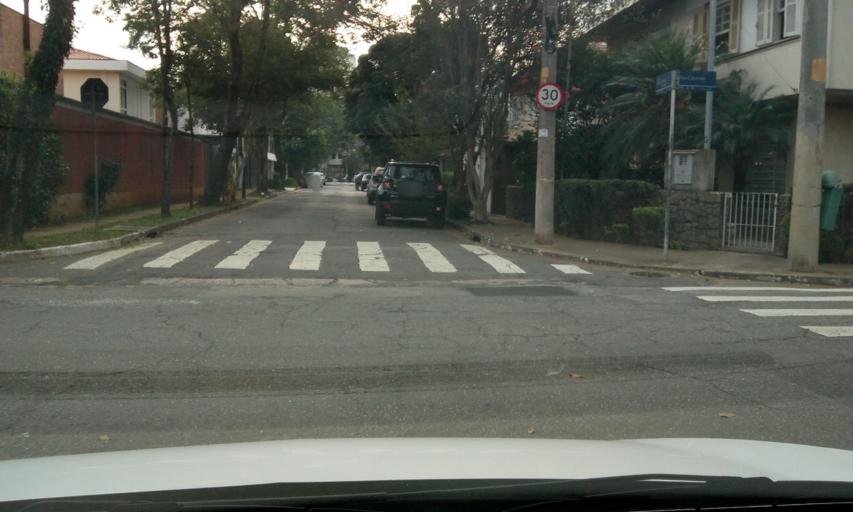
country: BR
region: Sao Paulo
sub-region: Sao Paulo
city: Sao Paulo
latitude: -23.6078
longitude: -46.6730
